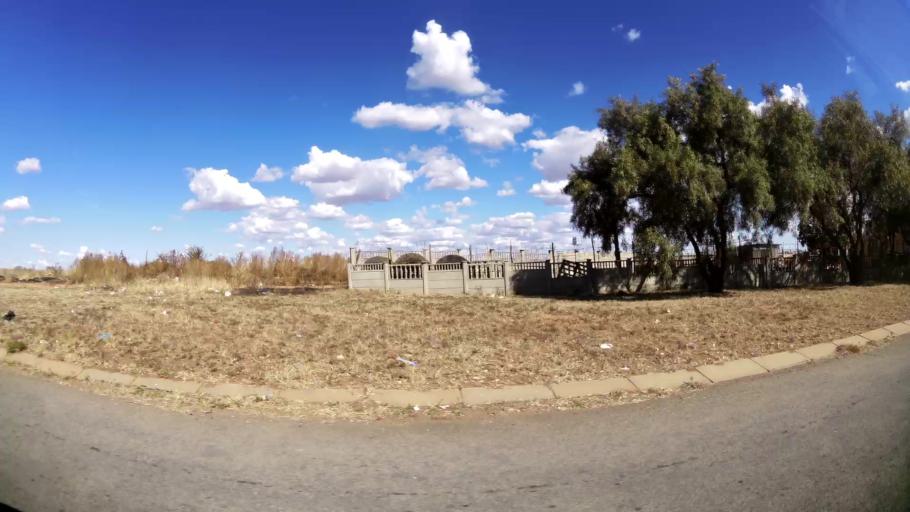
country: ZA
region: North-West
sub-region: Dr Kenneth Kaunda District Municipality
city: Klerksdorp
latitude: -26.8760
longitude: 26.5861
